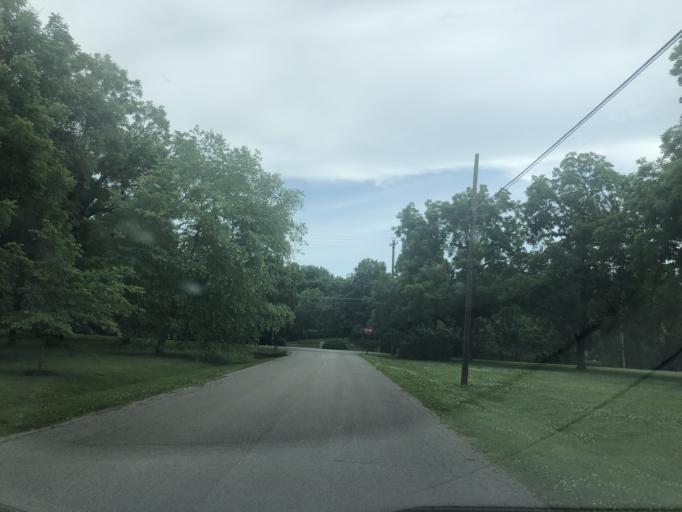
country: US
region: Tennessee
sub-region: Davidson County
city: Oak Hill
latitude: 36.1039
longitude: -86.7749
